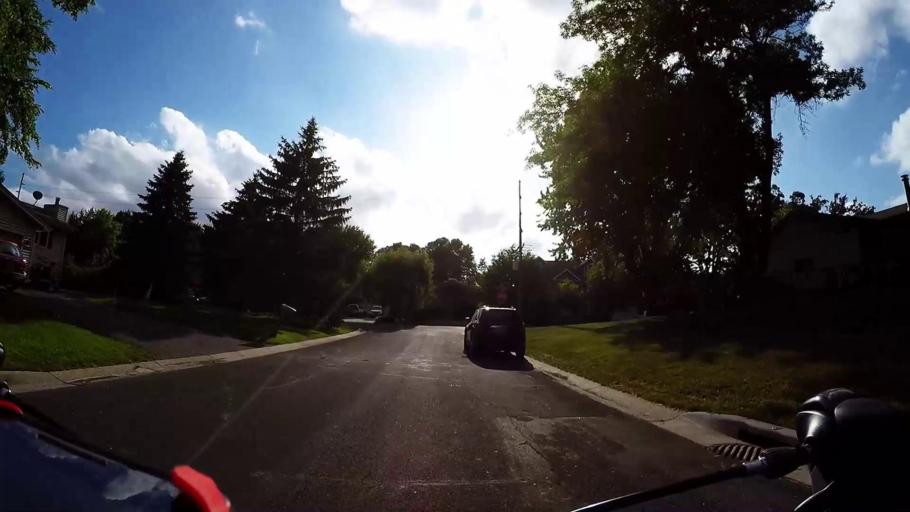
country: US
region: Minnesota
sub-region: Hennepin County
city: Minnetonka
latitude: 44.8815
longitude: -93.4953
